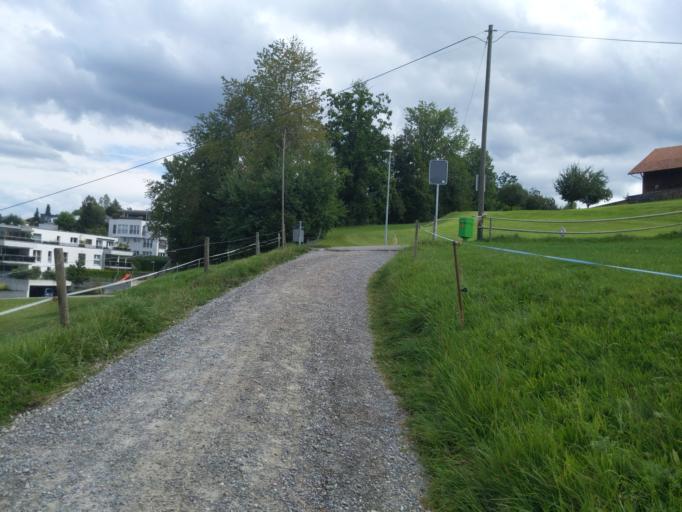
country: CH
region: Saint Gallen
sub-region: Wahlkreis St. Gallen
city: Gossau
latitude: 47.4075
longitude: 9.2458
